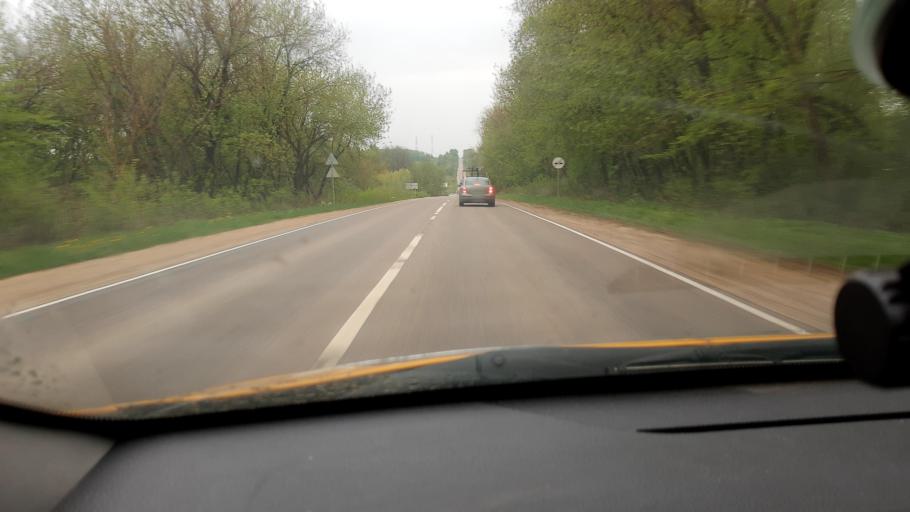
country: RU
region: Tula
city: Zaokskiy
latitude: 54.7853
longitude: 37.4339
